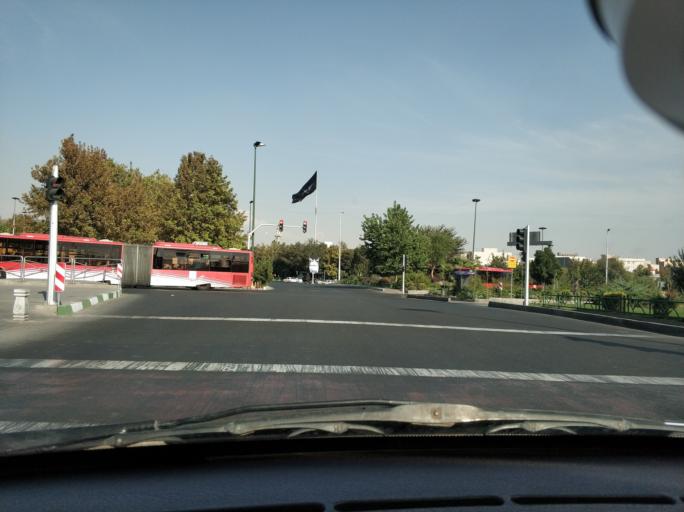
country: IR
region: Tehran
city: Tehran
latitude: 35.6977
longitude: 51.3379
